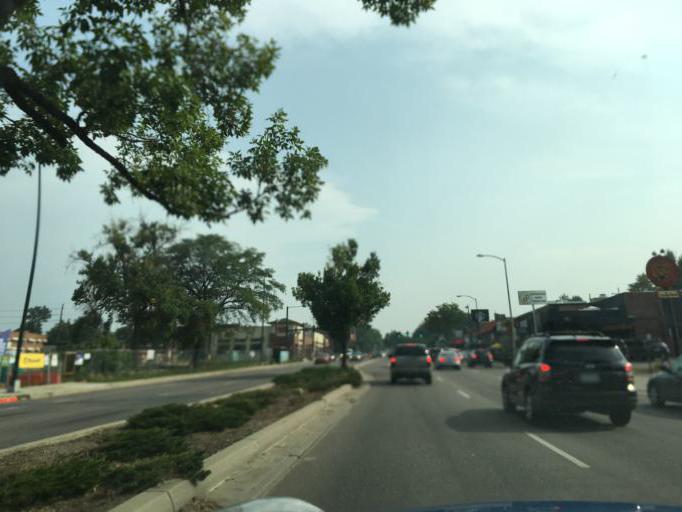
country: US
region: Colorado
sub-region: Arapahoe County
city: Glendale
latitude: 39.7305
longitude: -104.9407
